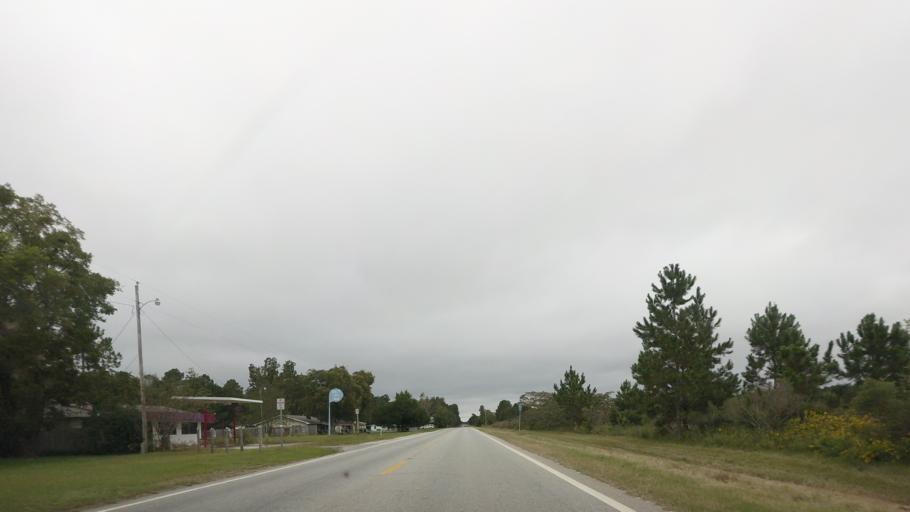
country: US
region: Georgia
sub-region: Berrien County
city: Ray City
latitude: 31.1136
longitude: -83.2109
